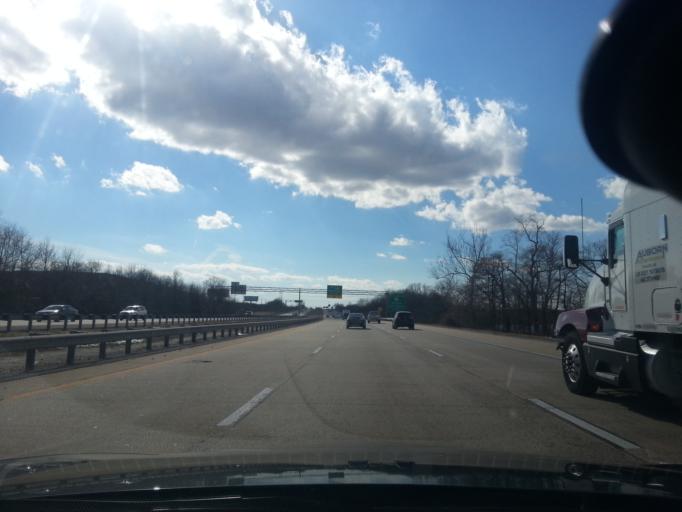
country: US
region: Delaware
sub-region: New Castle County
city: Wilmington Manor
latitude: 39.7168
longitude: -75.5680
